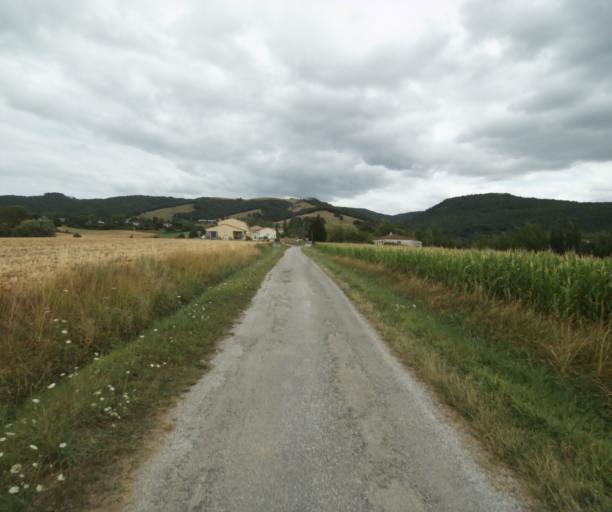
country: FR
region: Midi-Pyrenees
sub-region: Departement du Tarn
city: Soreze
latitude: 43.4593
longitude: 2.0688
